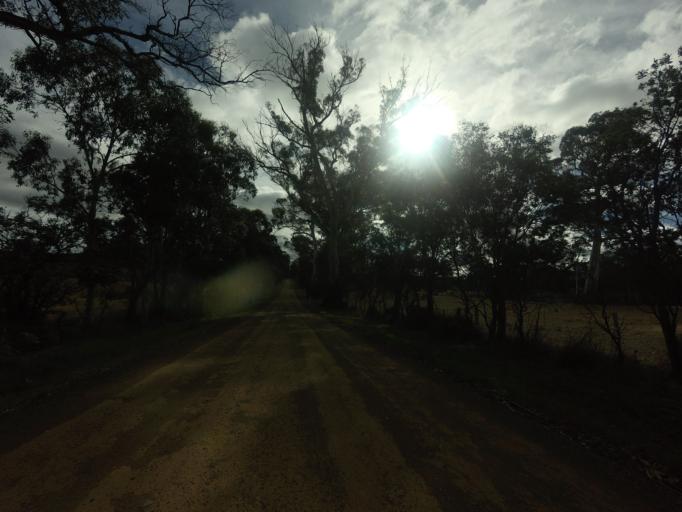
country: AU
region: Tasmania
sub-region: Brighton
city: Bridgewater
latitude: -42.4250
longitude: 147.4278
